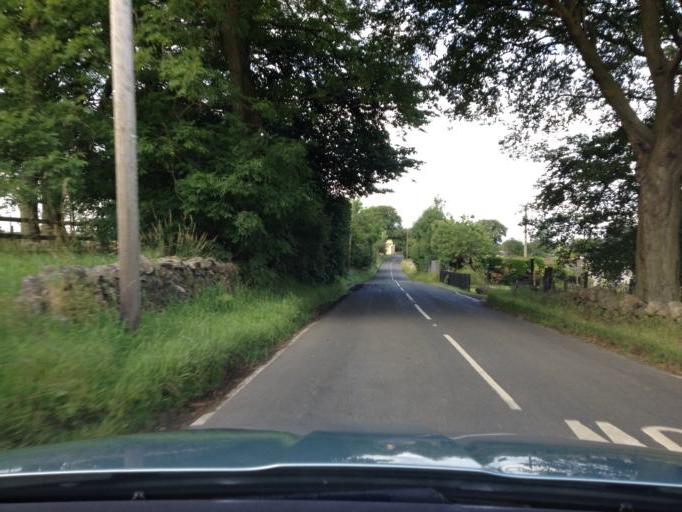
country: GB
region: Scotland
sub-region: West Lothian
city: Armadale
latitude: 55.9291
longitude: -3.7372
